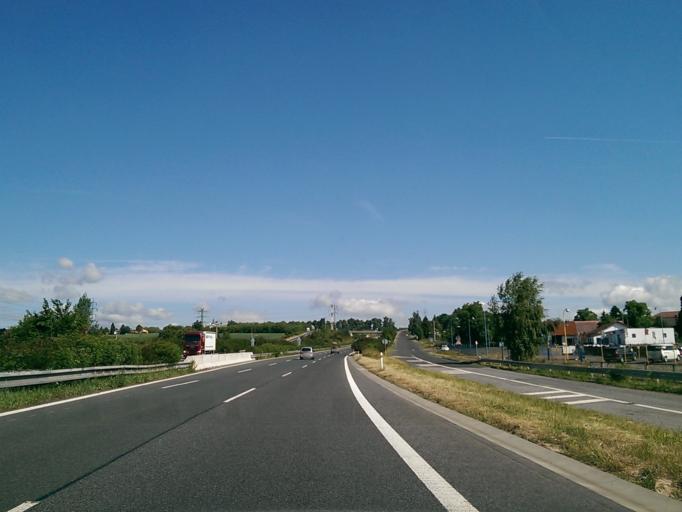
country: CZ
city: Ohrazenice
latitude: 50.6161
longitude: 15.1113
